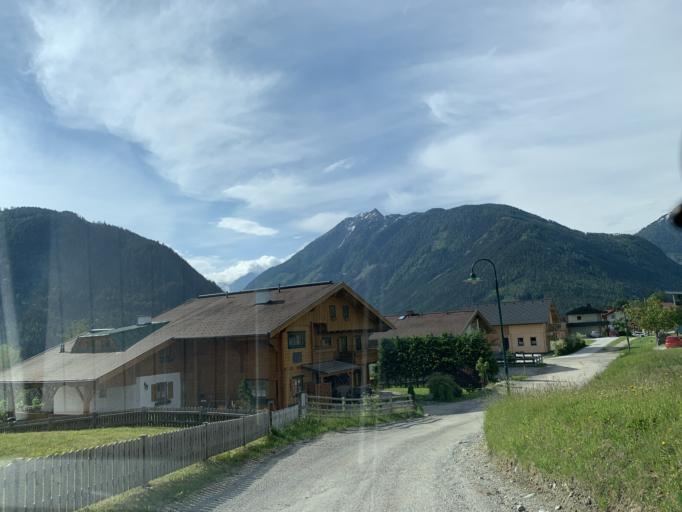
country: AT
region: Styria
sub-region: Politischer Bezirk Liezen
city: Schladming
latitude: 47.3817
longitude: 13.6702
